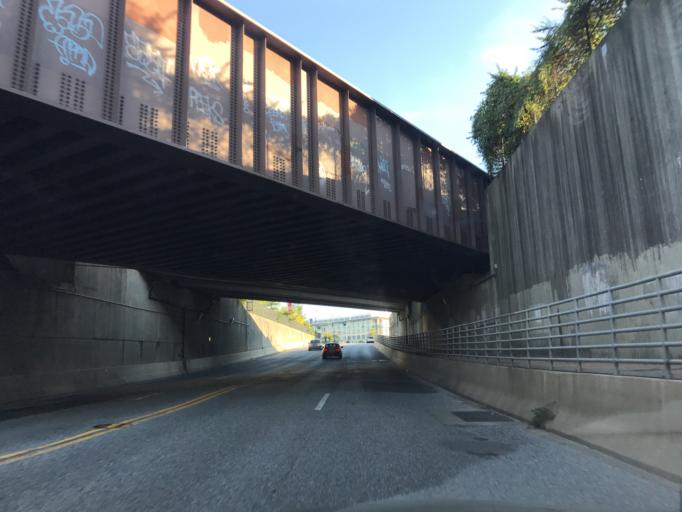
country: US
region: Maryland
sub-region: Prince George's County
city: College Park
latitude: 38.9815
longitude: -76.9276
